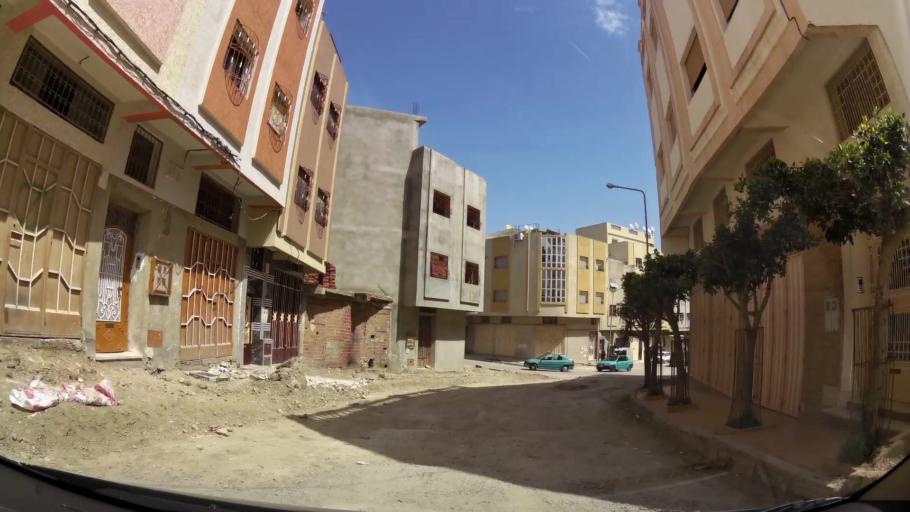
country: MA
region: Tanger-Tetouan
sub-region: Tanger-Assilah
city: Tangier
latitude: 35.7326
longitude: -5.8114
